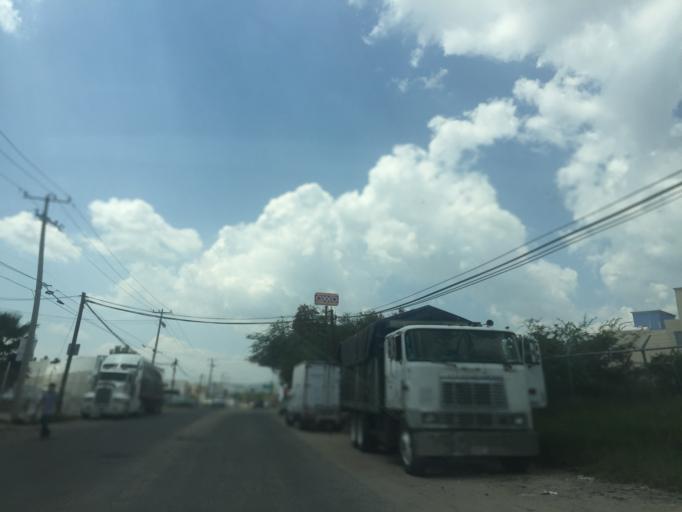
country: MX
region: Guanajuato
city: Leon
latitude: 21.1688
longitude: -101.6775
